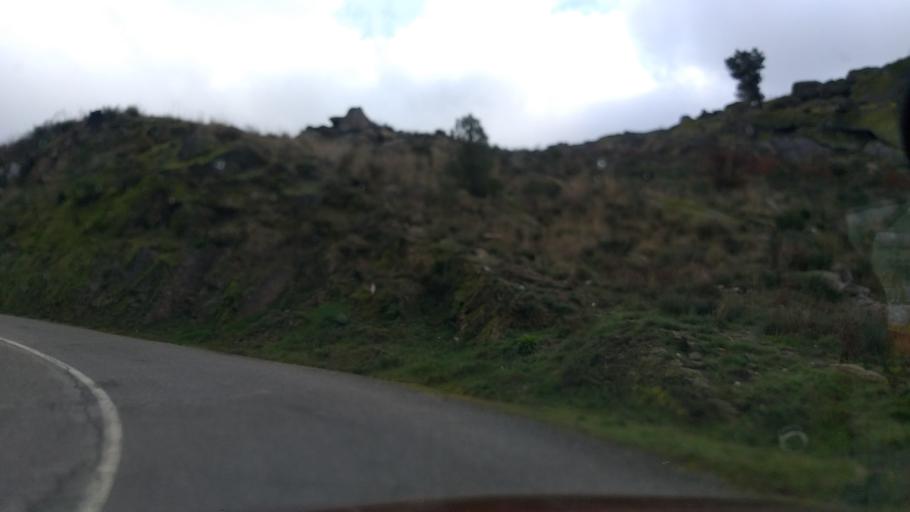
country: PT
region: Guarda
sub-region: Celorico da Beira
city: Celorico da Beira
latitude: 40.7112
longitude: -7.4216
